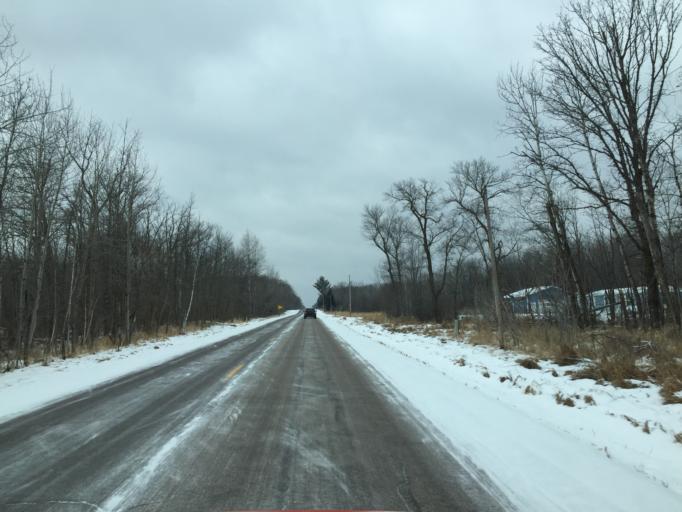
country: US
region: Minnesota
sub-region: Mille Lacs County
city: Vineland
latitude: 46.0776
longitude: -93.7560
